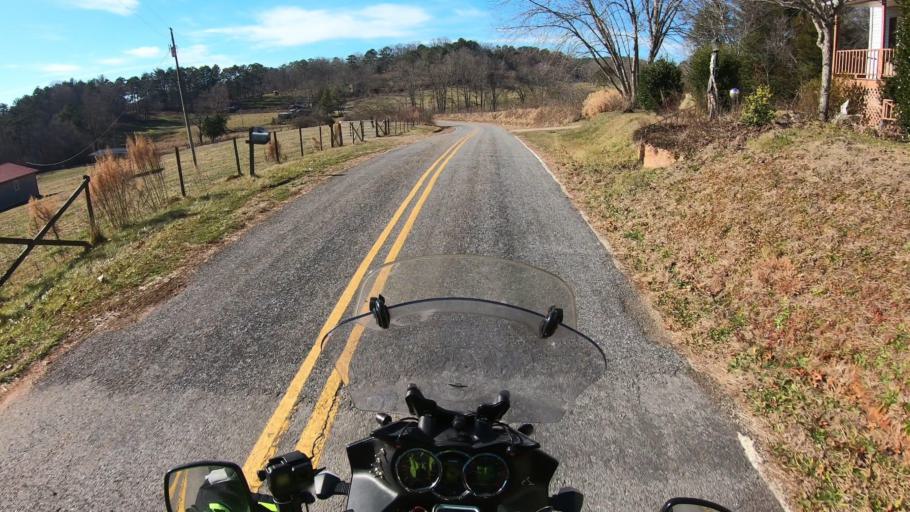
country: US
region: Georgia
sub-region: Fannin County
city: McCaysville
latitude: 34.9881
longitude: -84.3167
